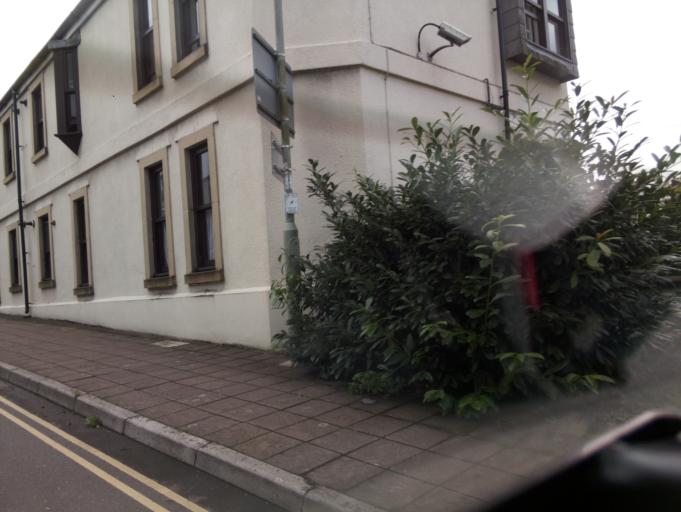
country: GB
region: England
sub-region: Devon
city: Modbury
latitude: 50.3487
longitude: -3.8862
